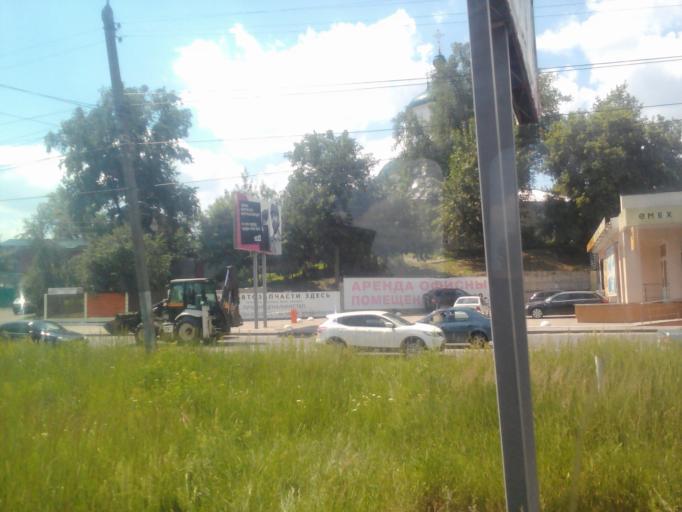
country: RU
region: Kursk
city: Kursk
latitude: 51.7211
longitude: 36.1887
